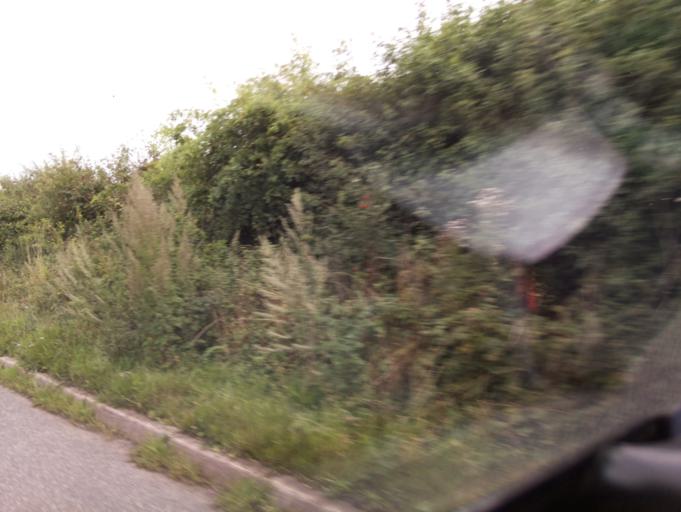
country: GB
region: England
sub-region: Devon
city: Bradninch
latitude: 50.8250
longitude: -3.3953
